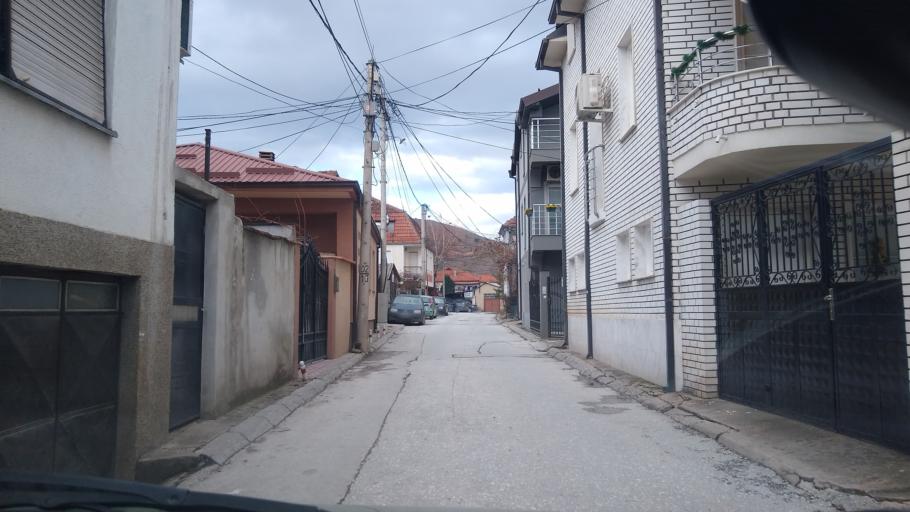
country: MK
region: Bitola
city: Bitola
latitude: 41.0301
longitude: 21.3237
